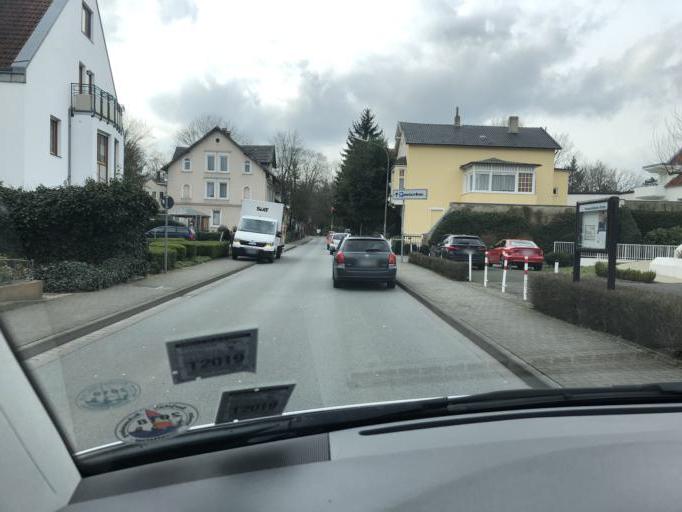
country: DE
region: North Rhine-Westphalia
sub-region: Regierungsbezirk Detmold
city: Herford
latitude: 52.1103
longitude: 8.6705
